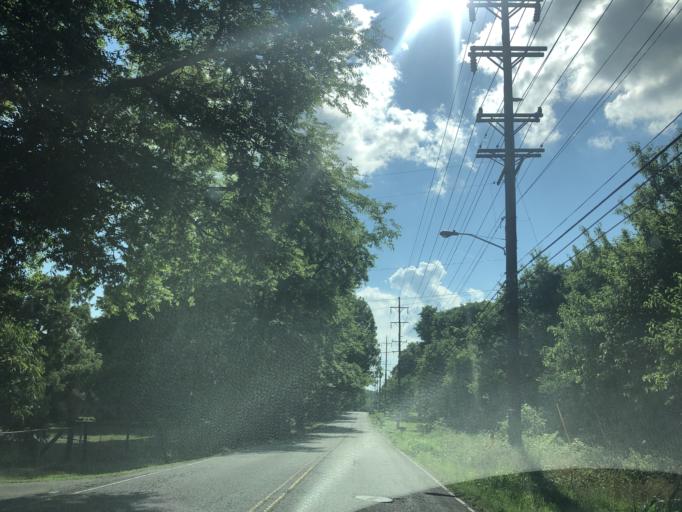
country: US
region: Tennessee
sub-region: Davidson County
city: Nashville
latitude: 36.2372
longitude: -86.8093
